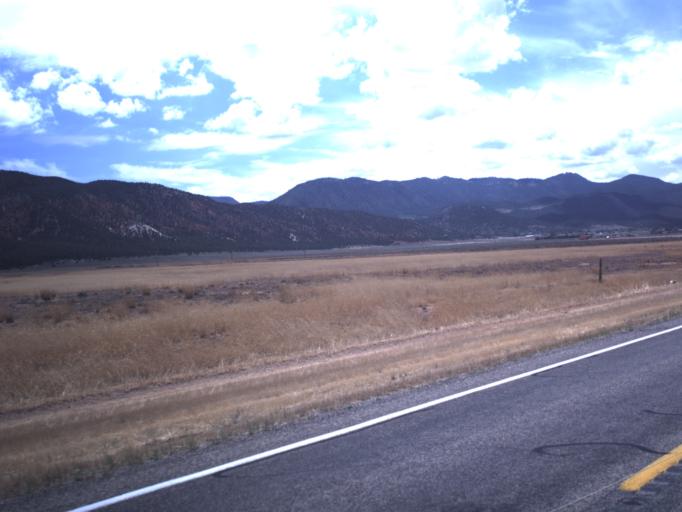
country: US
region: Utah
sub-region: Iron County
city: Parowan
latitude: 37.8673
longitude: -112.8002
